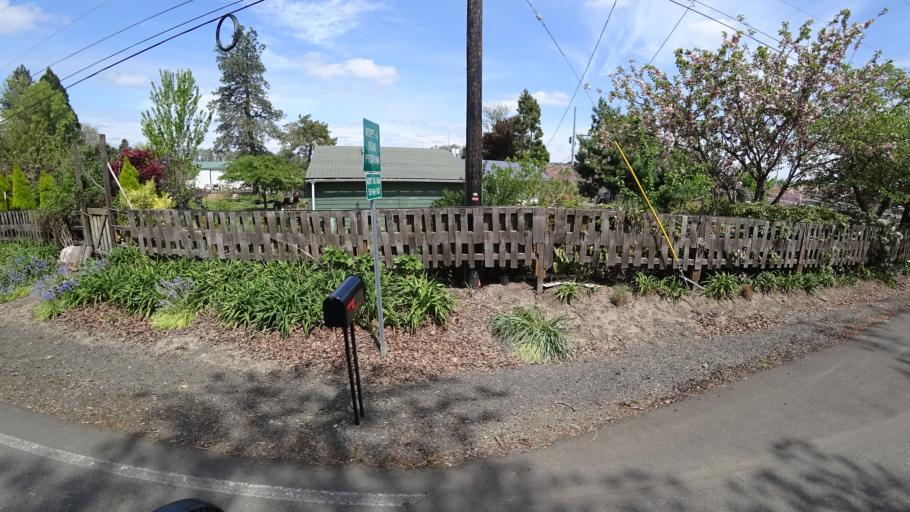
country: US
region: Oregon
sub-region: Washington County
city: Rockcreek
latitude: 45.5624
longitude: -122.9269
